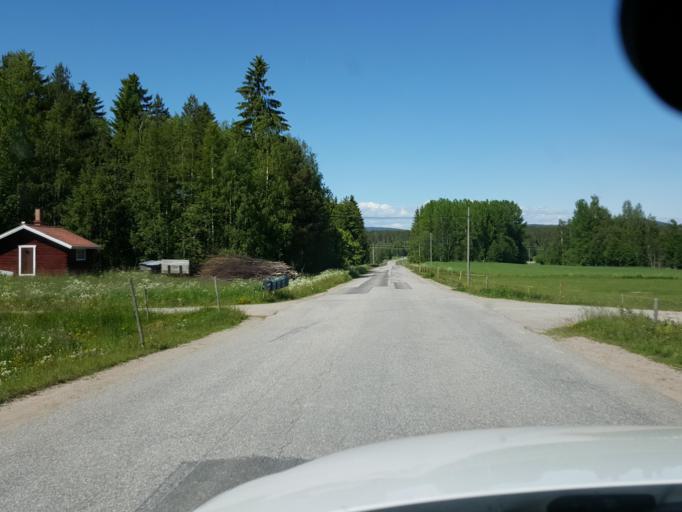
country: SE
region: Gaevleborg
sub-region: Ljusdals Kommun
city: Jaervsoe
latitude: 61.6727
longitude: 16.2983
